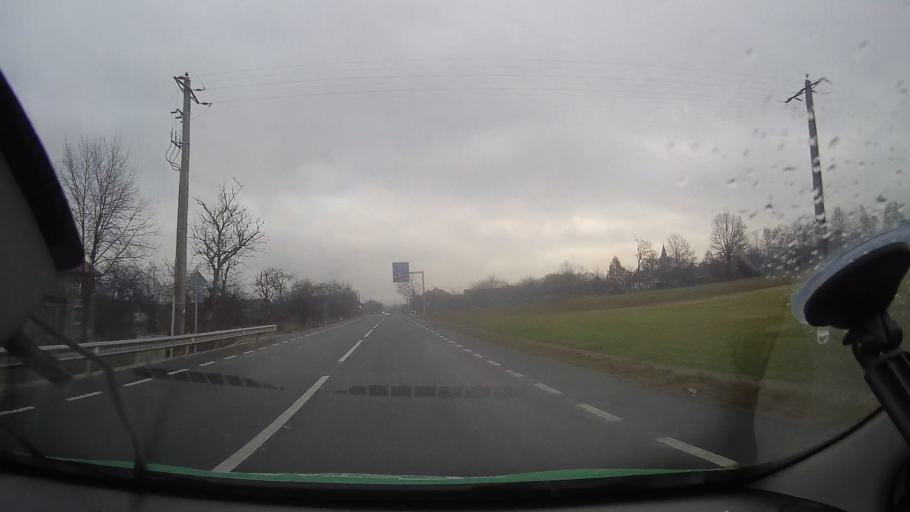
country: RO
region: Hunedoara
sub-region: Comuna Baia de Cris
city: Baia de Cris
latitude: 46.1726
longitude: 22.7118
